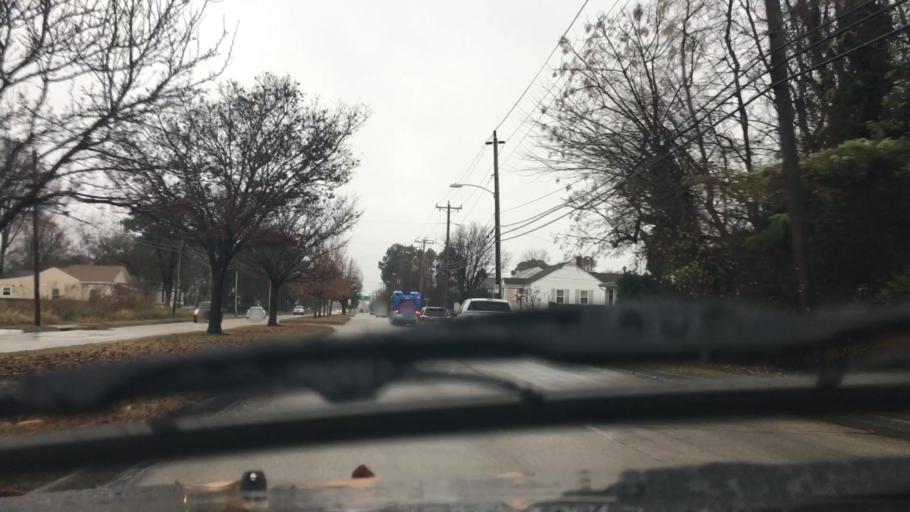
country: US
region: Virginia
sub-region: City of Norfolk
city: Norfolk
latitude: 36.9226
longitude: -76.2527
